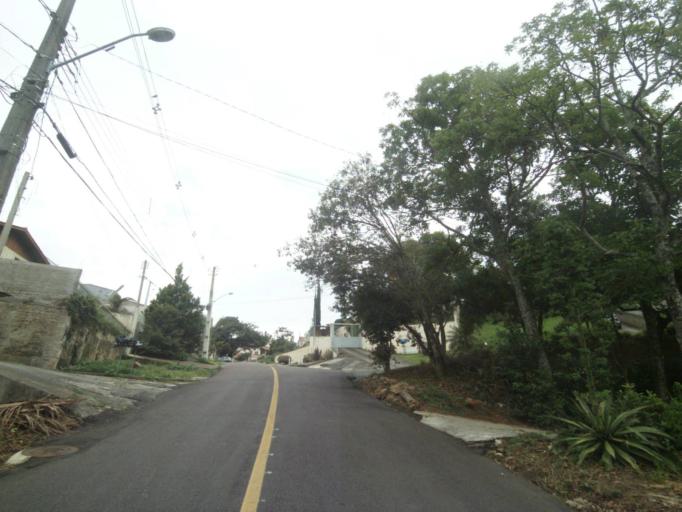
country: BR
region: Parana
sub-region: Curitiba
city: Curitiba
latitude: -25.3995
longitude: -49.3025
